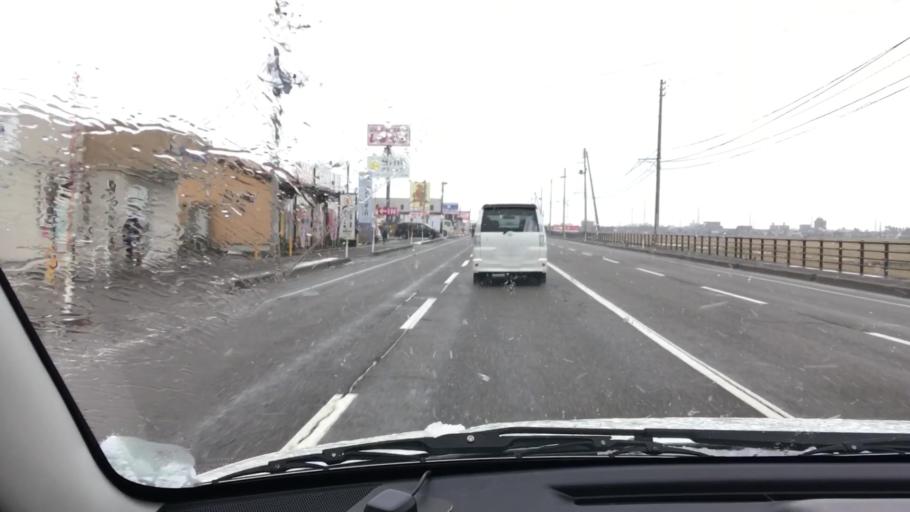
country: JP
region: Niigata
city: Joetsu
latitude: 37.1251
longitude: 138.2321
